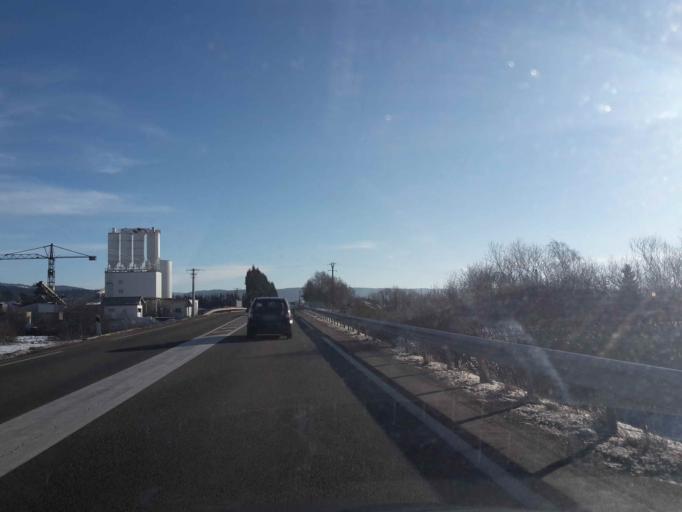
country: FR
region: Franche-Comte
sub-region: Departement du Doubs
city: Doubs
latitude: 46.9446
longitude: 6.3428
